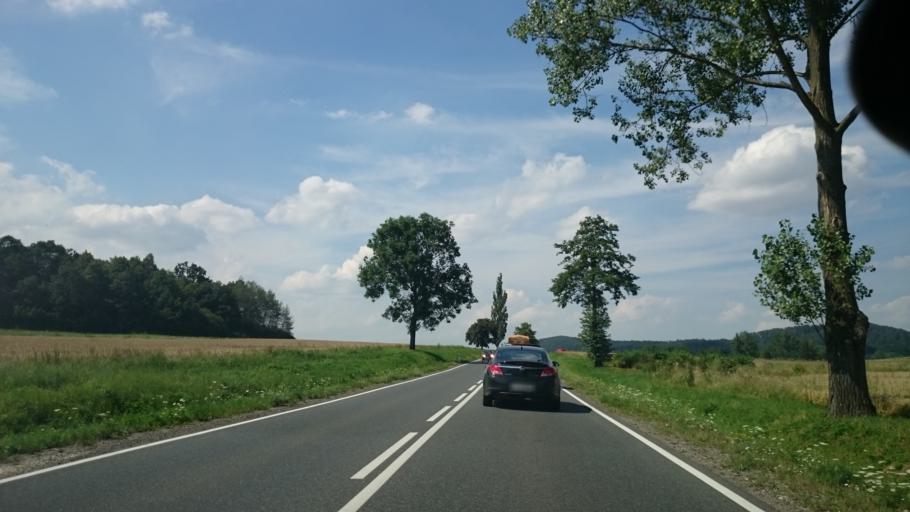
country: PL
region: Lower Silesian Voivodeship
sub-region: Powiat klodzki
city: Bystrzyca Klodzka
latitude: 50.3375
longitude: 16.6625
